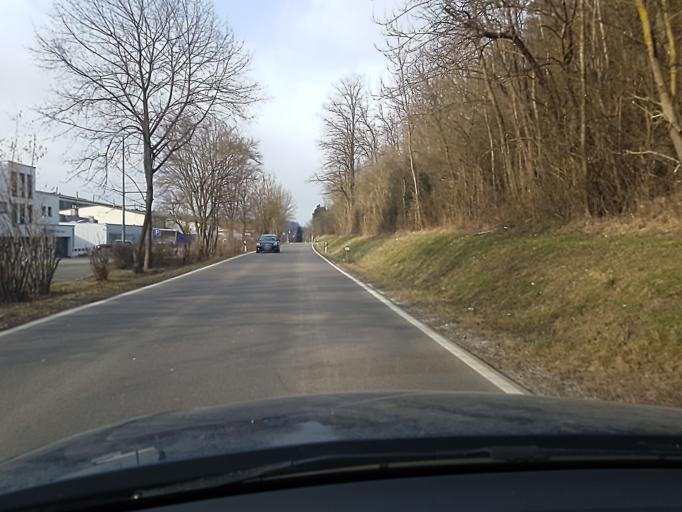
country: DE
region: Baden-Wuerttemberg
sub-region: Regierungsbezirk Stuttgart
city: Eberdingen
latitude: 48.8699
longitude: 8.9673
